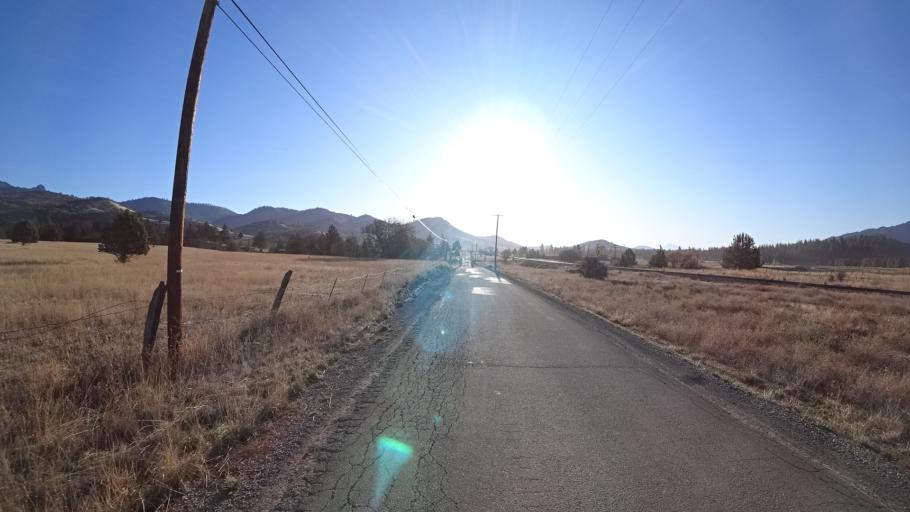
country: US
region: Oregon
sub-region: Jackson County
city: Ashland
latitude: 42.0002
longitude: -122.6356
